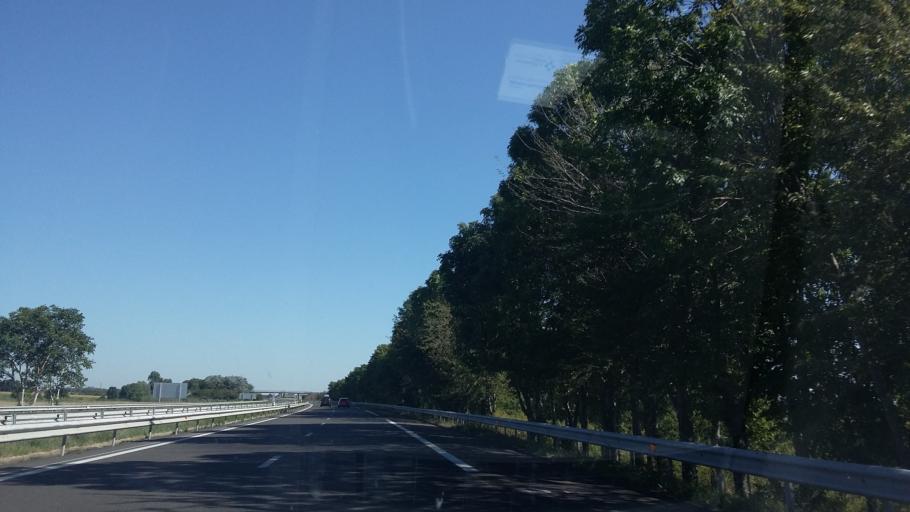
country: FR
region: Auvergne
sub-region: Departement du Puy-de-Dome
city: Pont-du-Chateau
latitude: 45.8103
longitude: 3.2214
